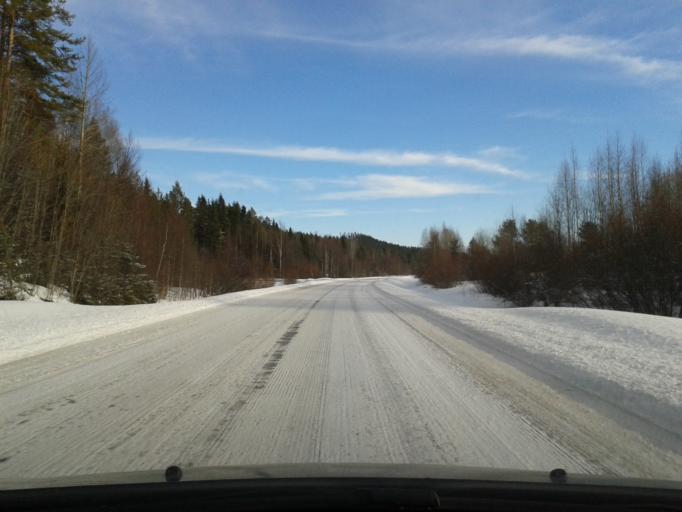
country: SE
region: Vaesterbotten
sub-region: Asele Kommun
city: Asele
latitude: 64.3231
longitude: 17.0908
